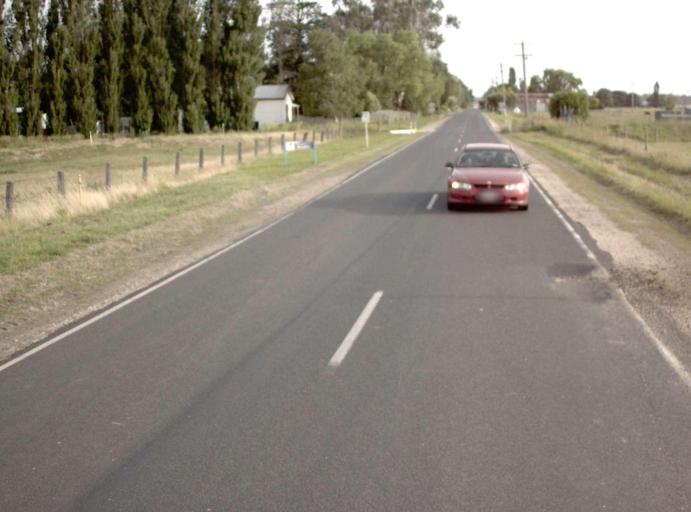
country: AU
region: Victoria
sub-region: Wellington
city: Heyfield
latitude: -37.8805
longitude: 146.9874
